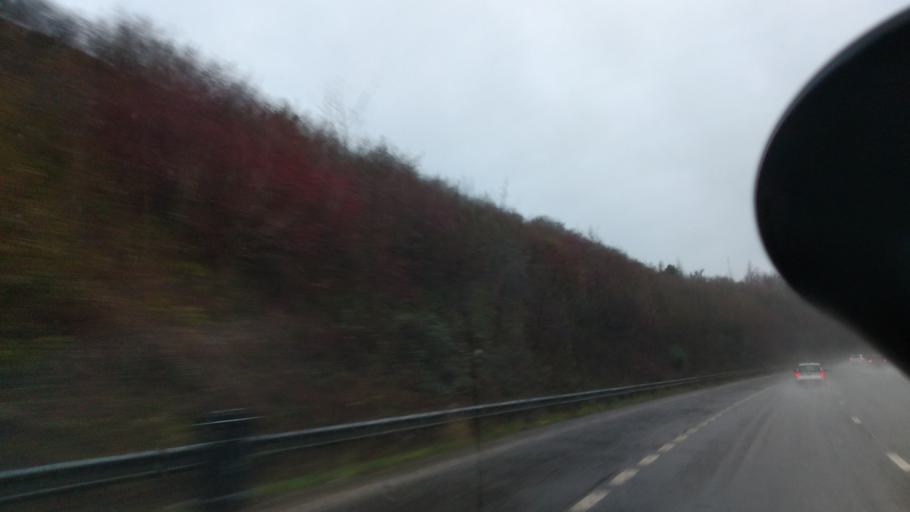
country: GB
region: England
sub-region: Brighton and Hove
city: Brighton
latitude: 50.8600
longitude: -0.0993
